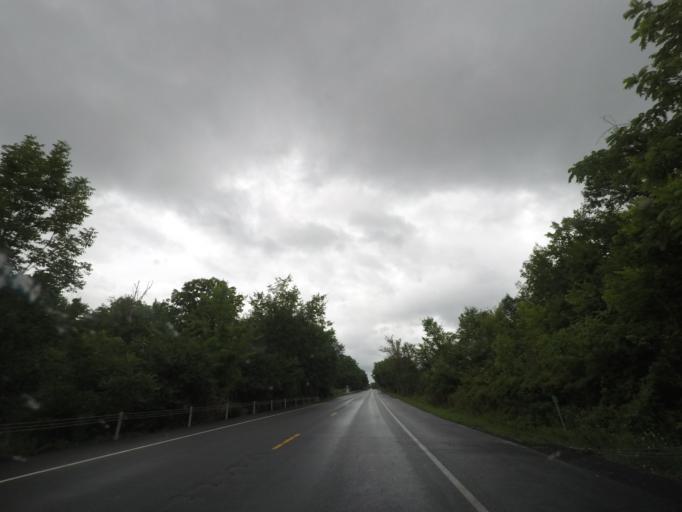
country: US
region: New York
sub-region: Rensselaer County
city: Hampton Manor
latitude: 42.6202
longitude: -73.7088
